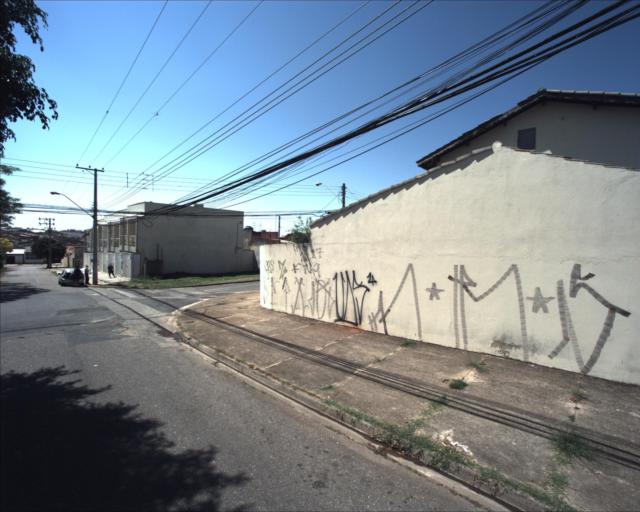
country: BR
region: Sao Paulo
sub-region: Sorocaba
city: Sorocaba
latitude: -23.4675
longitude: -47.4839
